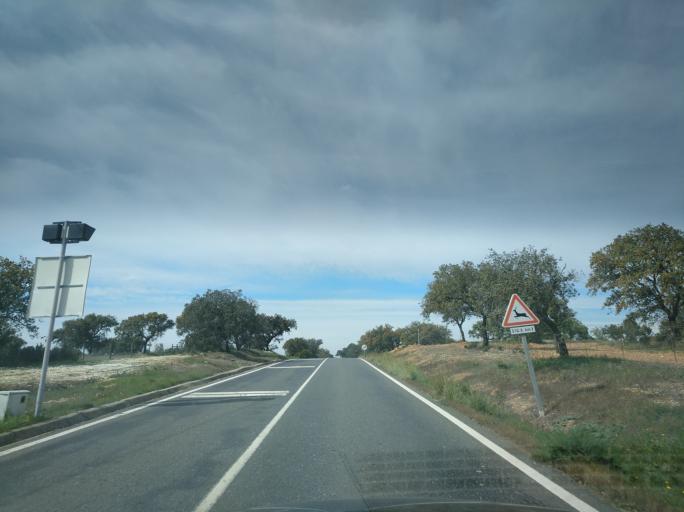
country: PT
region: Beja
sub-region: Mertola
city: Mertola
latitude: 37.7460
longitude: -7.7967
